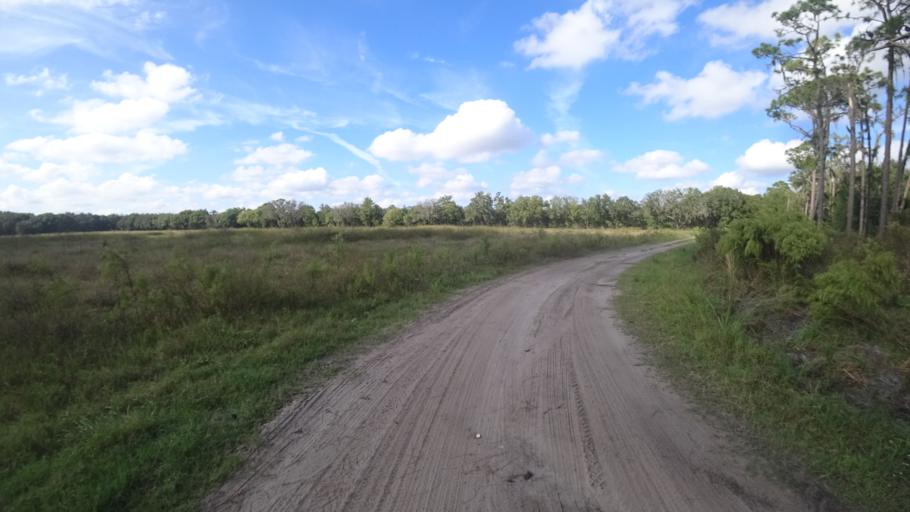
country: US
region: Florida
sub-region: DeSoto County
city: Arcadia
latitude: 27.3524
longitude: -82.1173
